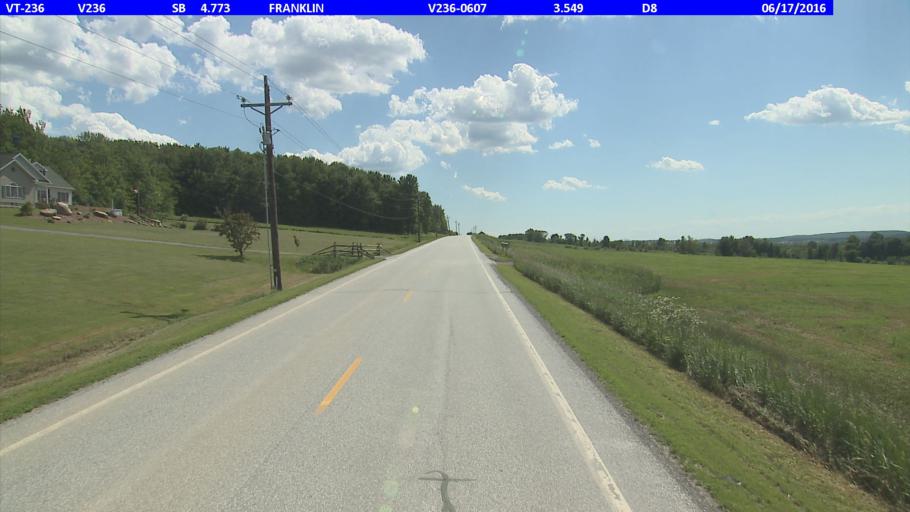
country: US
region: Vermont
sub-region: Franklin County
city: Enosburg Falls
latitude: 44.9766
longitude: -72.8468
